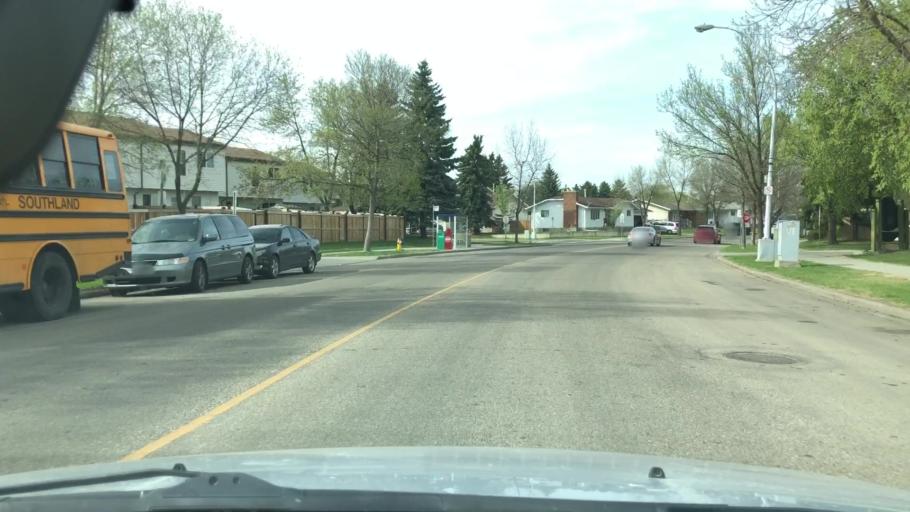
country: CA
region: Alberta
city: Edmonton
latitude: 53.6031
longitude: -113.5303
